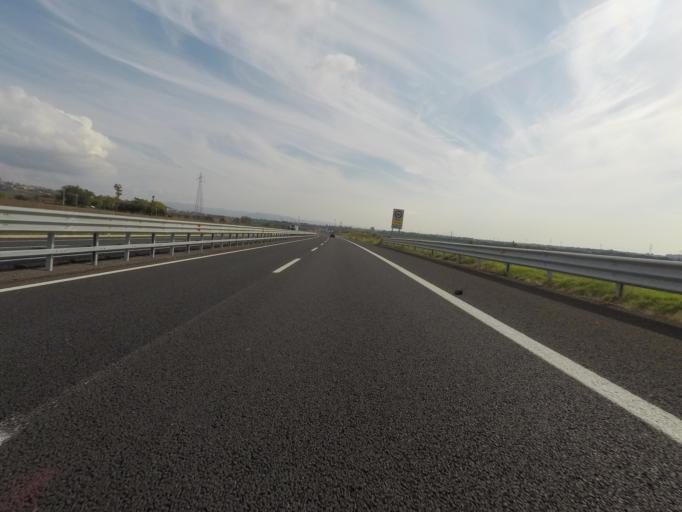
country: IT
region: Latium
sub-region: Provincia di Viterbo
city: Tarquinia
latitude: 42.2621
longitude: 11.7236
